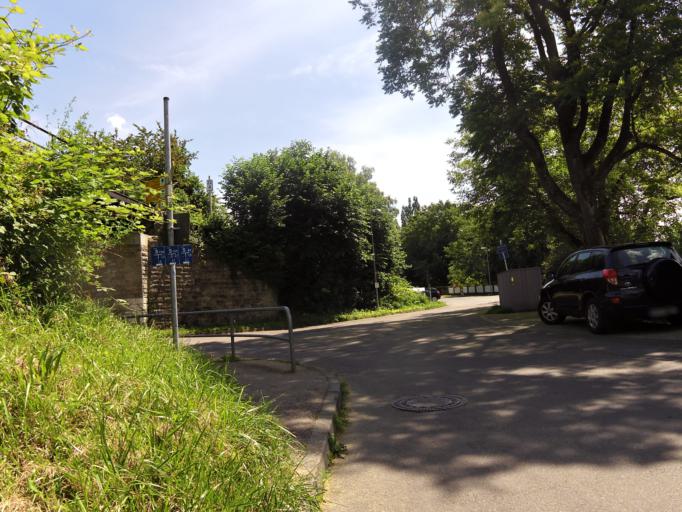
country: DE
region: Baden-Wuerttemberg
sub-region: Tuebingen Region
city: Uberlingen
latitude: 47.7509
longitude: 9.1991
